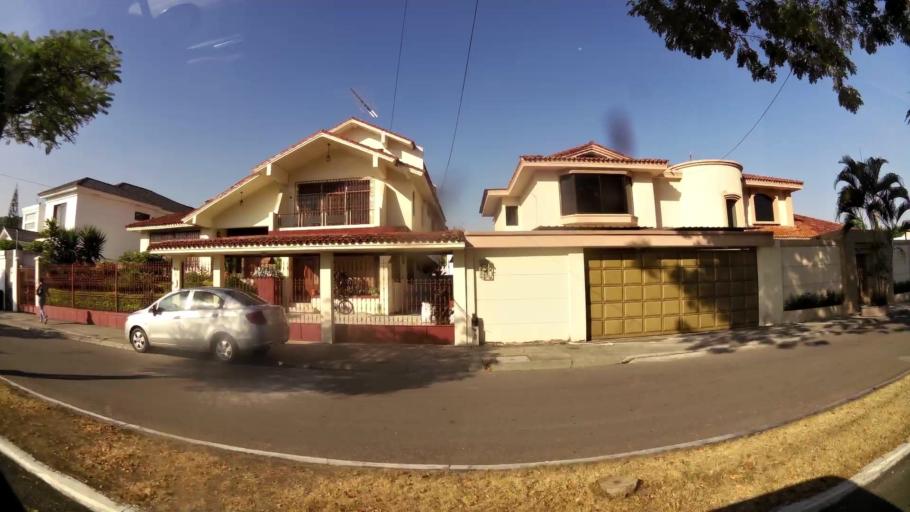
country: EC
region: Guayas
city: Santa Lucia
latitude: -2.1906
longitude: -79.9678
